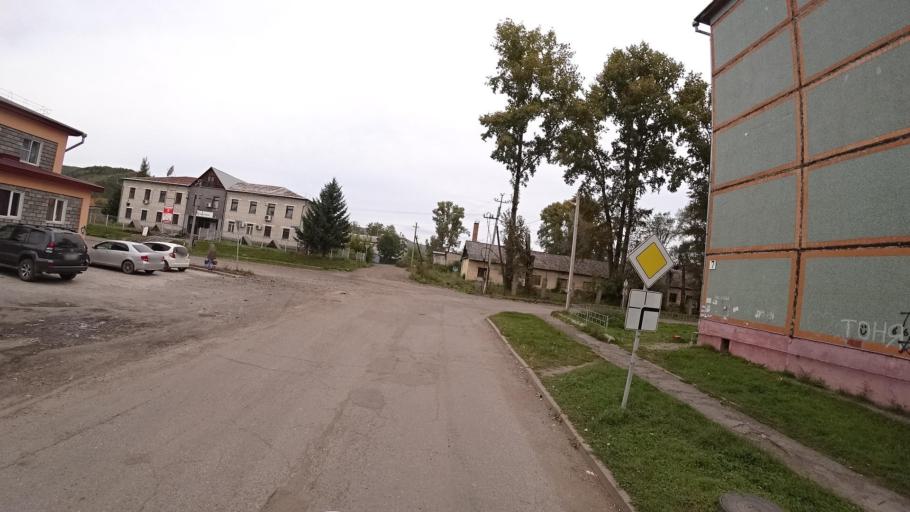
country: RU
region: Jewish Autonomous Oblast
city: Khingansk
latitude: 49.0103
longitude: 131.0523
